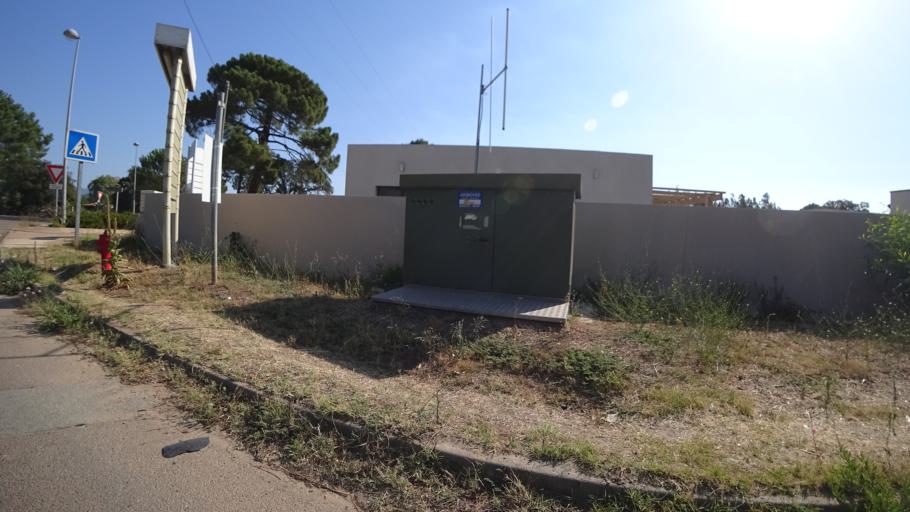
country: FR
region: Corsica
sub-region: Departement de la Corse-du-Sud
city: Porto-Vecchio
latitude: 41.6321
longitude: 9.3313
